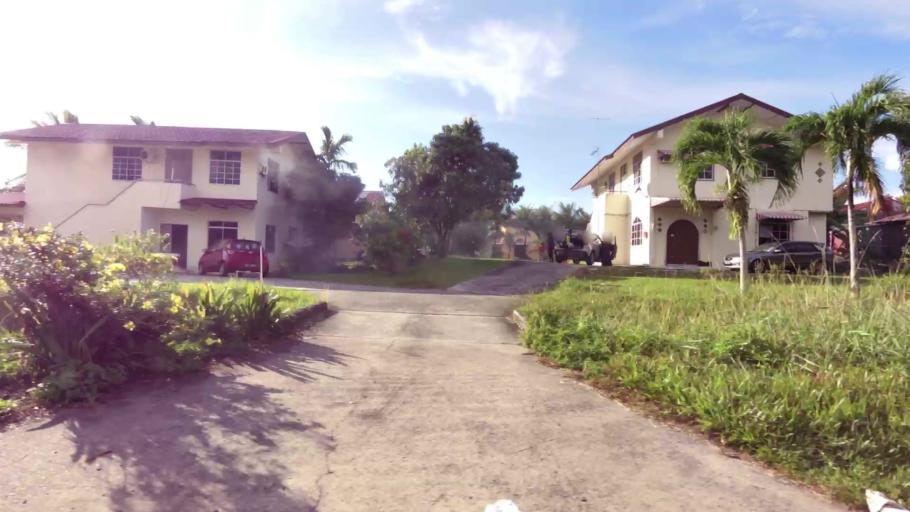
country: BN
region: Brunei and Muara
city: Bandar Seri Begawan
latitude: 4.9853
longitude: 114.9671
